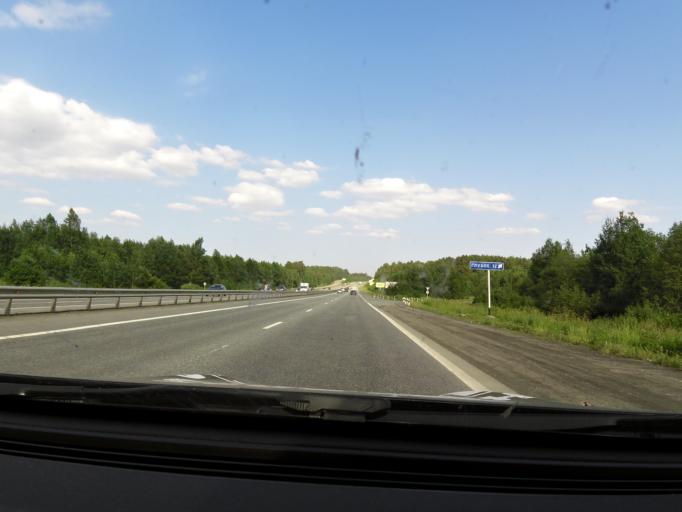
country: RU
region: Sverdlovsk
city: Severka
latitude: 56.8318
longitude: 60.3596
